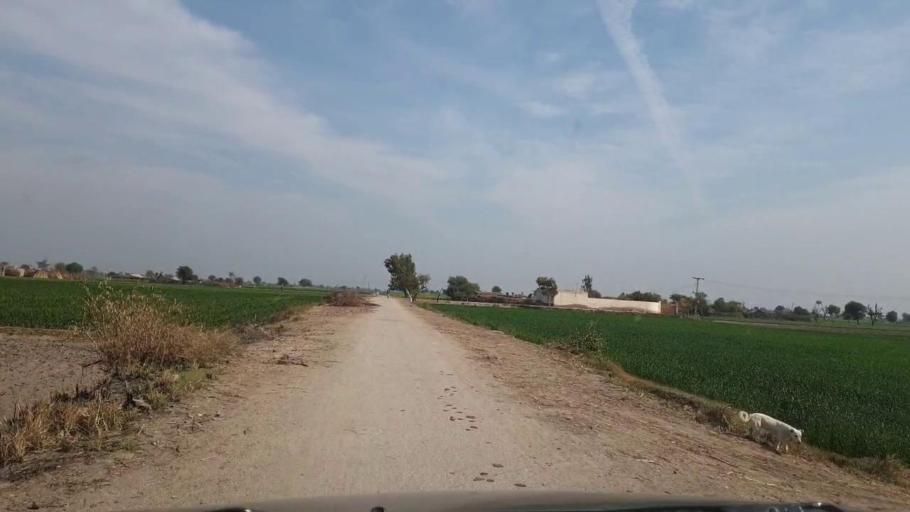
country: PK
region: Sindh
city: Khadro
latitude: 26.1216
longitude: 68.7247
